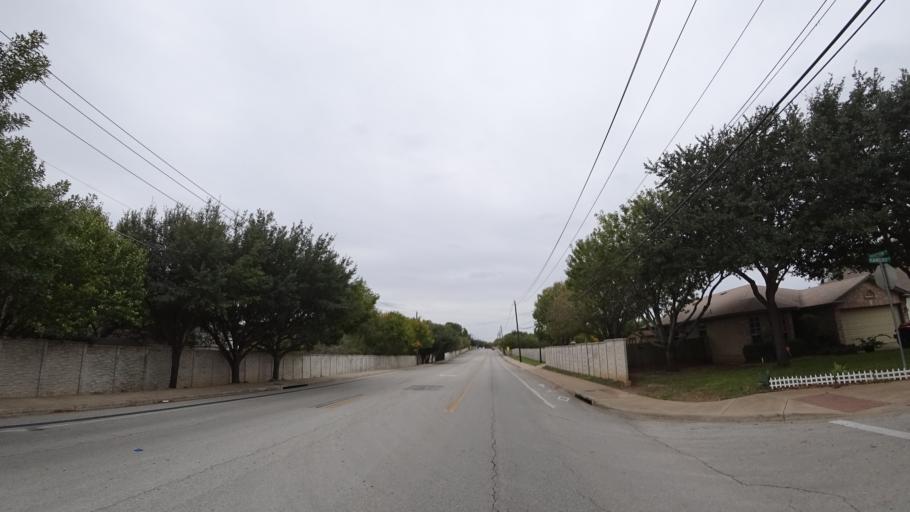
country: US
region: Texas
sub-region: Travis County
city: Wells Branch
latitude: 30.4485
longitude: -97.6847
